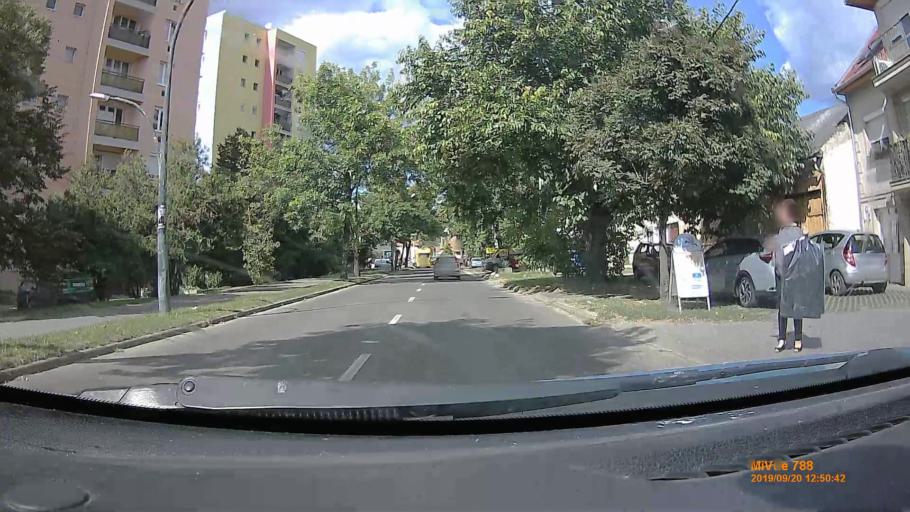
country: HU
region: Heves
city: Eger
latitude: 47.8971
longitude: 20.3861
